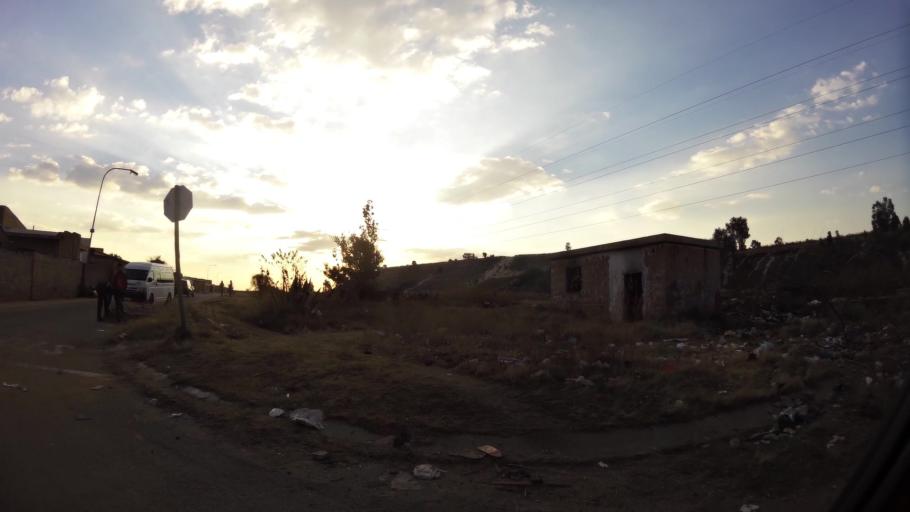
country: ZA
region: Gauteng
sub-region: City of Johannesburg Metropolitan Municipality
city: Roodepoort
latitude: -26.2077
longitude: 27.8962
